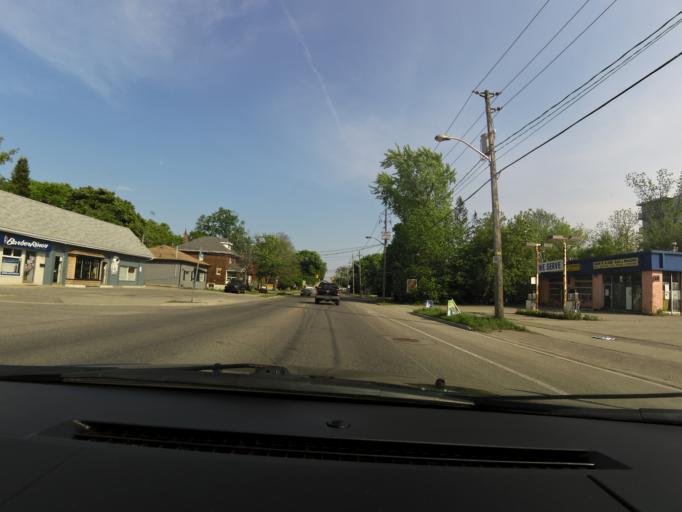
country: CA
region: Ontario
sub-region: Wellington County
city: Guelph
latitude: 43.5561
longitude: -80.2651
